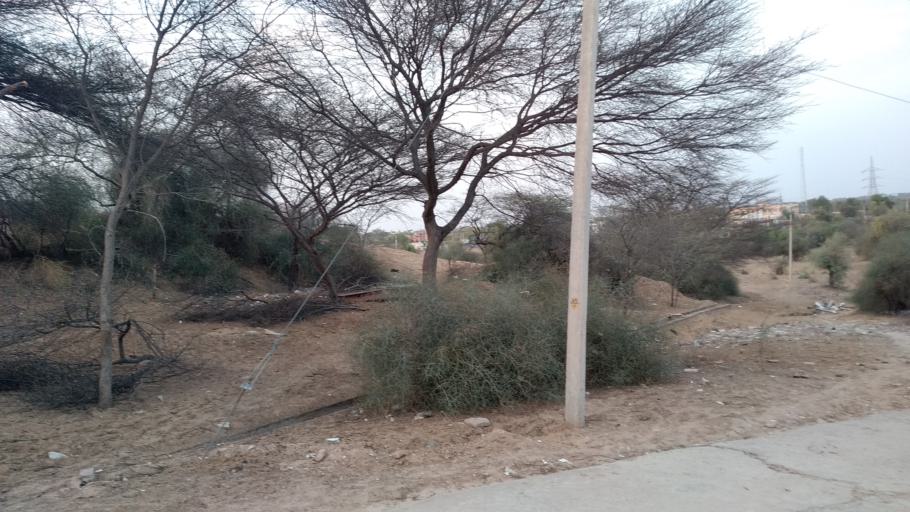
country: IN
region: Rajasthan
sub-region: Sikar
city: Fatehpur
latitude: 28.0409
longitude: 75.1494
